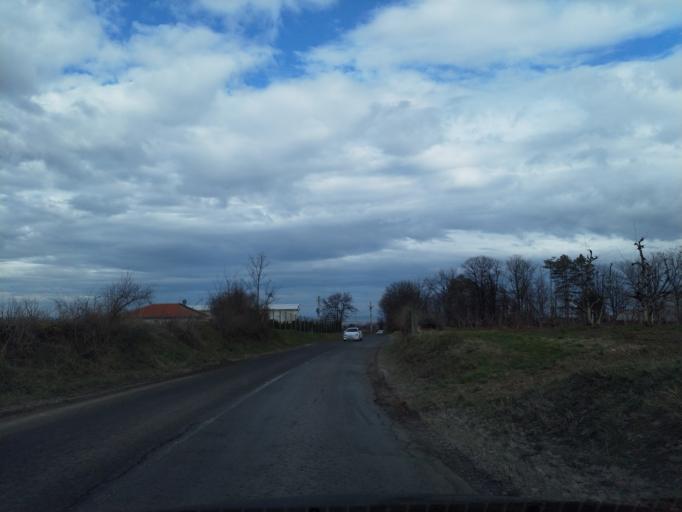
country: RS
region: Central Serbia
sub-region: Belgrade
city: Grocka
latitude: 44.6408
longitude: 20.7509
